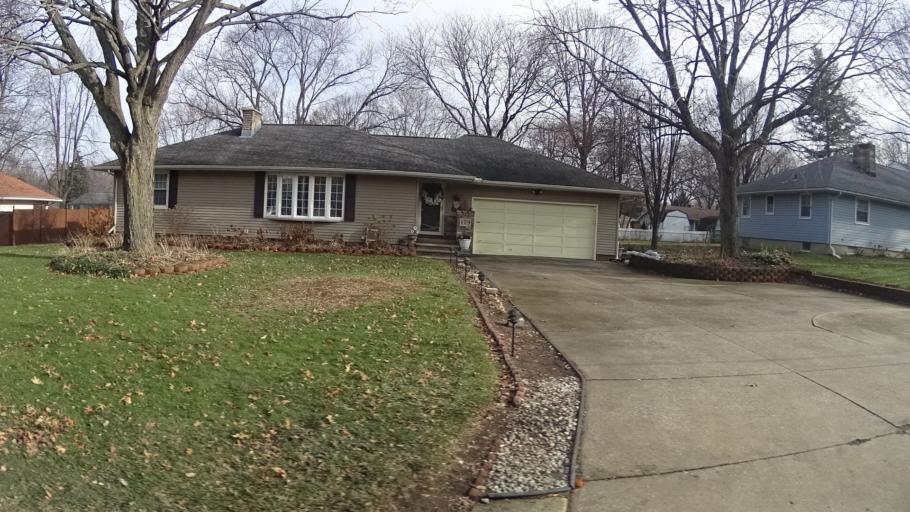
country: US
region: Ohio
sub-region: Lorain County
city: Amherst
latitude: 41.3997
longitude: -82.2095
